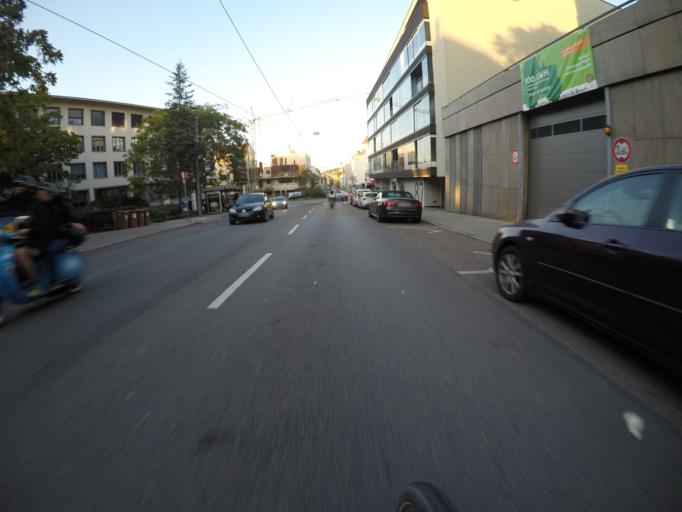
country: DE
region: Baden-Wuerttemberg
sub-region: Regierungsbezirk Stuttgart
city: Stuttgart
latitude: 48.7695
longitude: 9.1807
